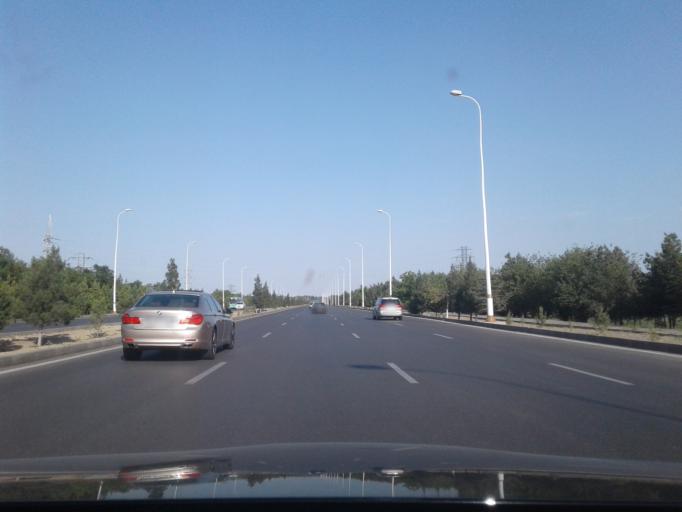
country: TM
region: Ahal
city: Abadan
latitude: 38.0124
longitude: 58.2716
